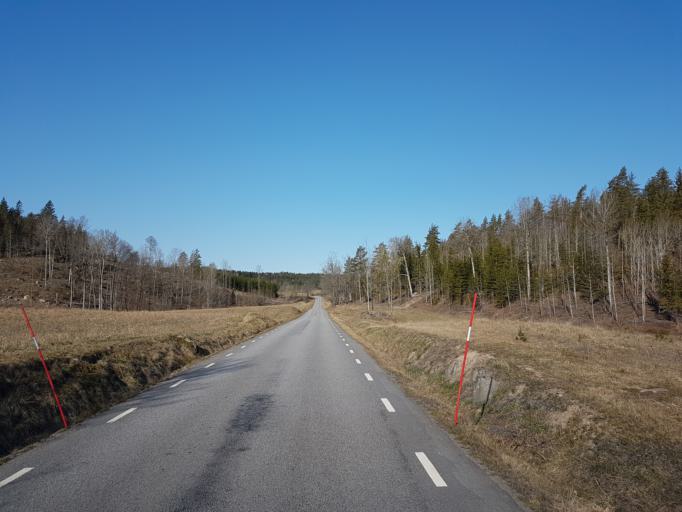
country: SE
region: OEstergoetland
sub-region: Valdemarsviks Kommun
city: Gusum
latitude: 58.1995
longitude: 16.3602
